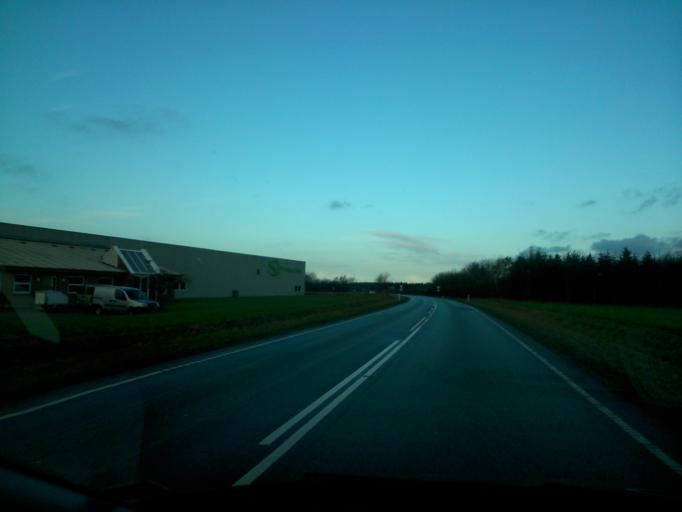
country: DK
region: Central Jutland
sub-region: Ringkobing-Skjern Kommune
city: Videbaek
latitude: 56.0890
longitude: 8.6493
